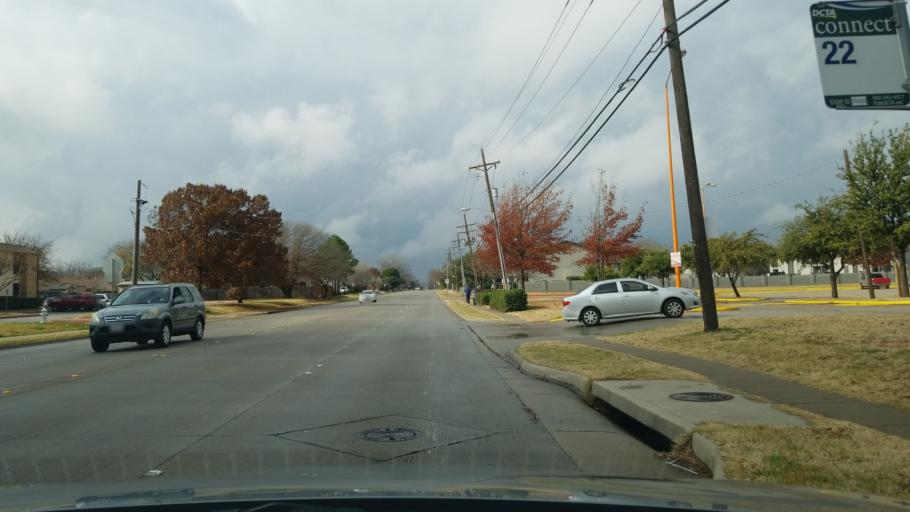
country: US
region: Texas
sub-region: Denton County
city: Lewisville
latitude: 33.0349
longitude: -97.0119
